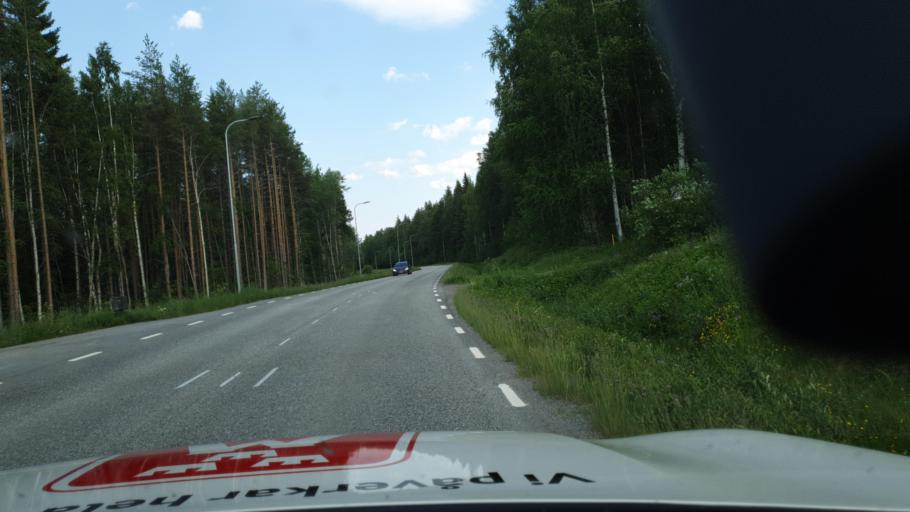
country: SE
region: Vaesterbotten
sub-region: Skelleftea Kommun
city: Viken
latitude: 64.7378
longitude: 20.7587
